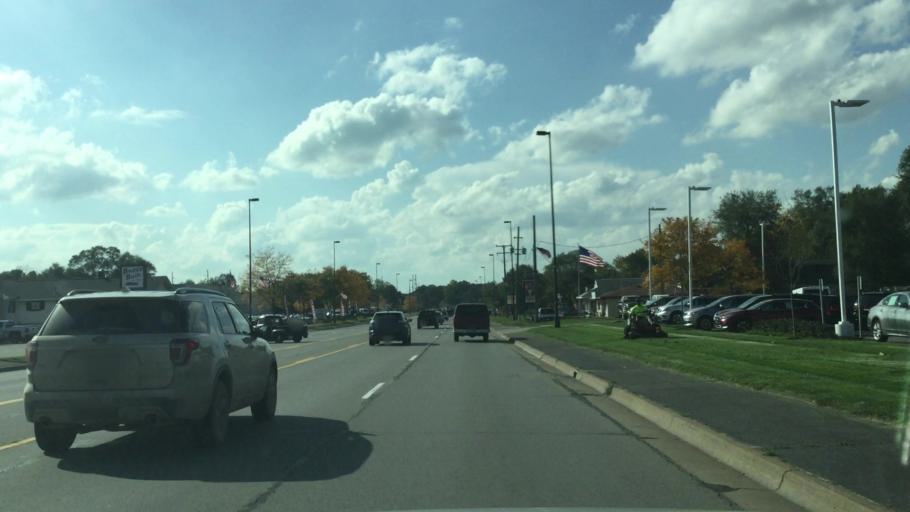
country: US
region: Michigan
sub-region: Oakland County
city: Milford
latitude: 42.6538
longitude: -83.5782
